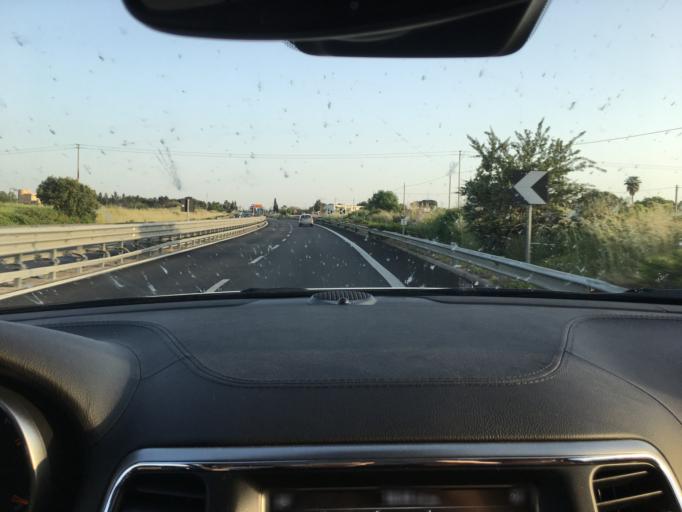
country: IT
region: Apulia
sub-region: Provincia di Lecce
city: San Pietro in Lama
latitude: 40.2978
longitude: 18.1320
